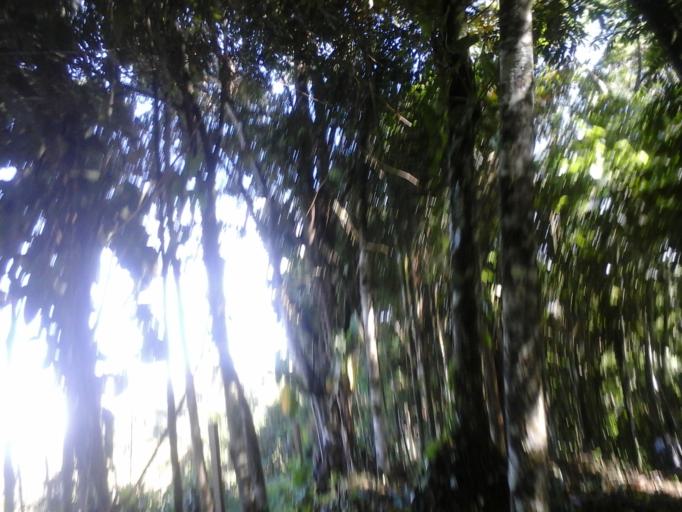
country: CO
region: Putumayo
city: Orito
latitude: 0.6464
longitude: -76.8183
